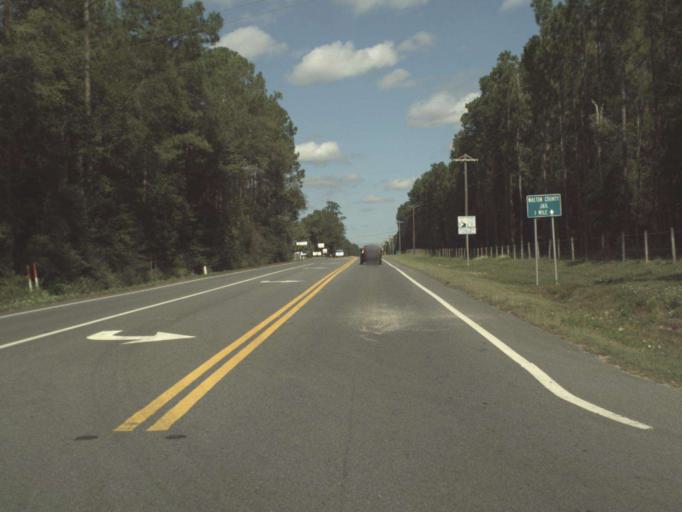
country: US
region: Florida
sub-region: Walton County
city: DeFuniak Springs
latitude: 30.7752
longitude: -86.1145
